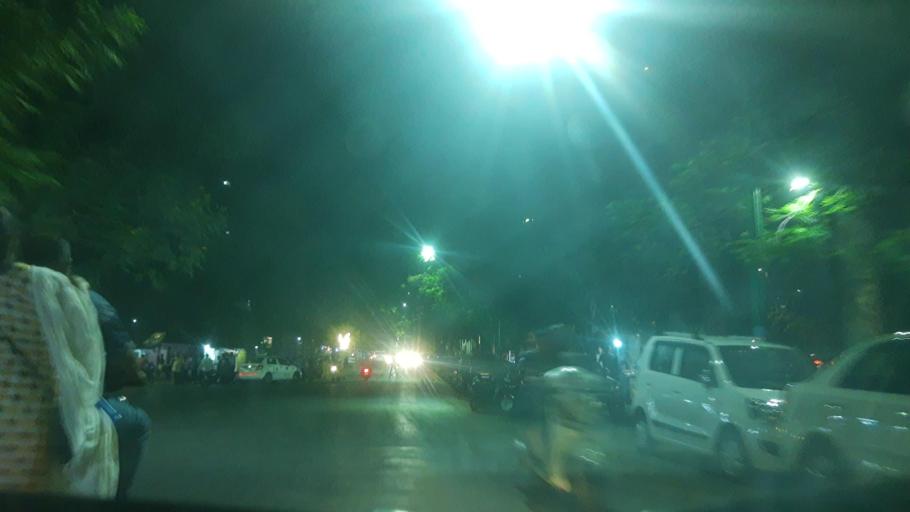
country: IN
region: Maharashtra
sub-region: Thane
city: Thane
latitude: 19.2083
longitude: 72.9733
